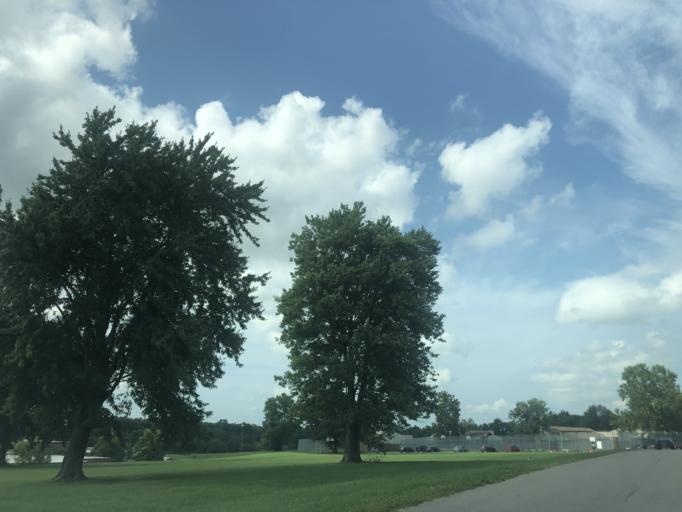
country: US
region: Tennessee
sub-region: Davidson County
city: Lakewood
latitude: 36.1636
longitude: -86.6453
